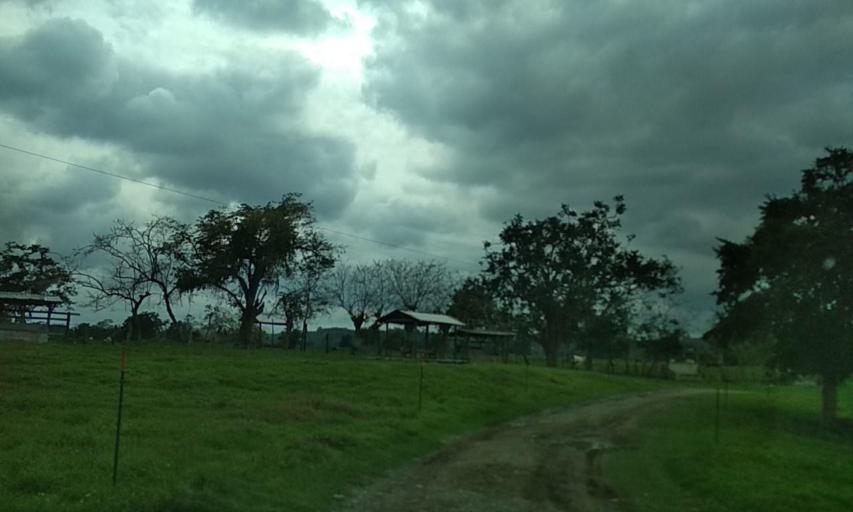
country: MX
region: Veracruz
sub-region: Papantla
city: El Chote
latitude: 20.3915
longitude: -97.3422
